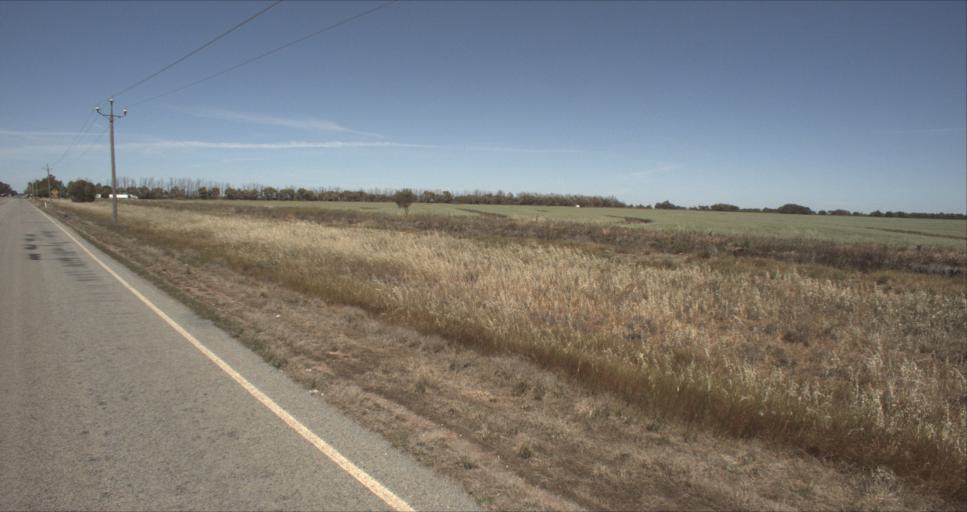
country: AU
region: New South Wales
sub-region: Leeton
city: Leeton
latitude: -34.5161
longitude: 146.2842
